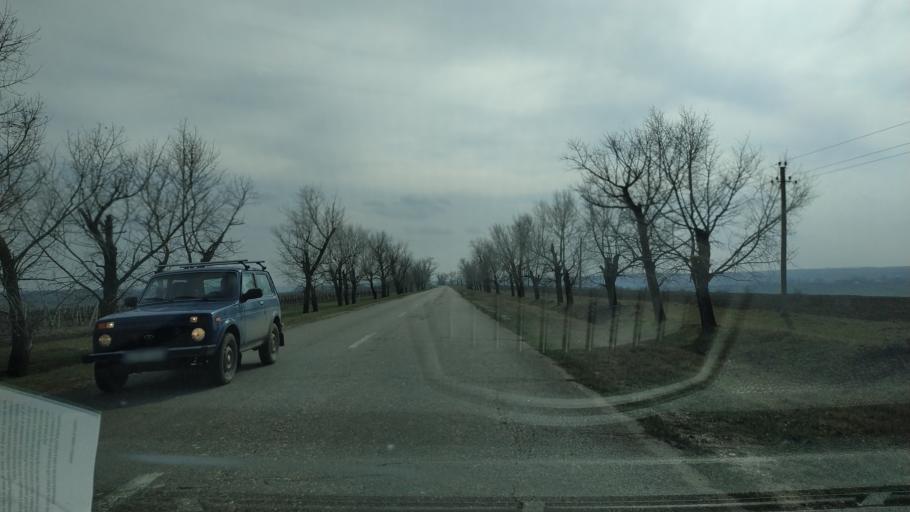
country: MD
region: Gagauzia
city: Vulcanesti
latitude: 45.7086
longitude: 28.4006
